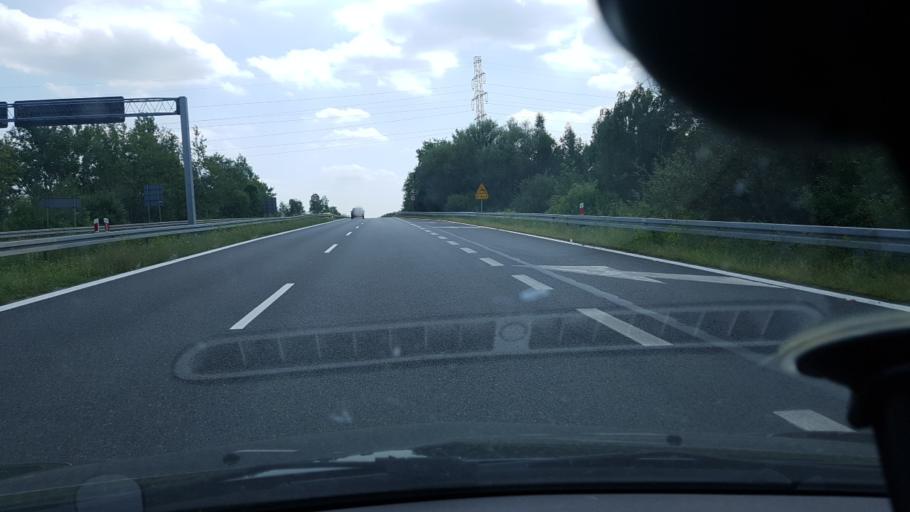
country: PL
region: Silesian Voivodeship
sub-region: Powiat bierunsko-ledzinski
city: Bierun
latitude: 50.1031
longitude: 19.0948
